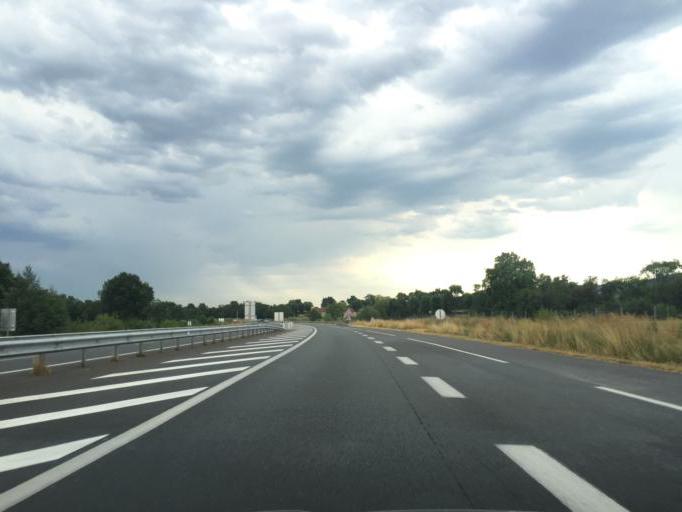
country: FR
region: Rhone-Alpes
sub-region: Departement de la Loire
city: Ambierle
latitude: 46.1367
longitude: 3.8998
